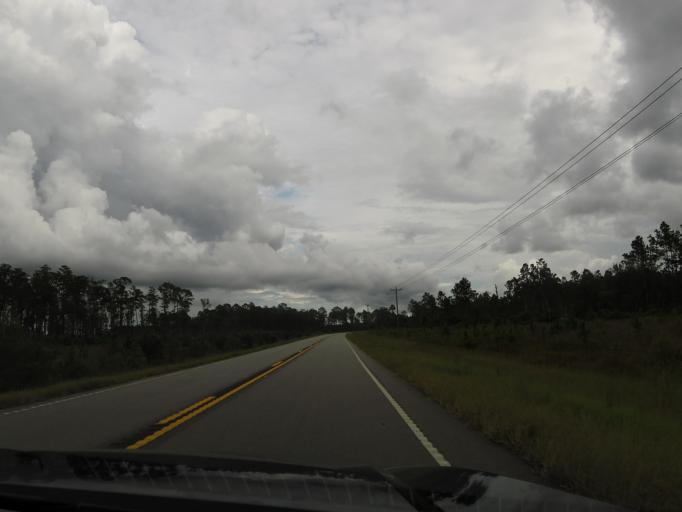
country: US
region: Florida
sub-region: Baker County
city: Macclenny
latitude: 30.5238
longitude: -82.1595
